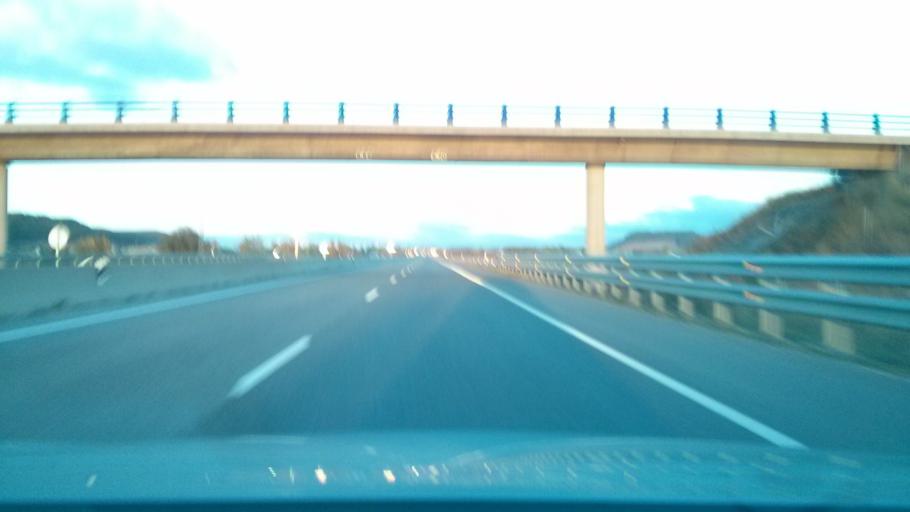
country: ES
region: Castille and Leon
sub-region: Provincia de Burgos
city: Villalbilla de Burgos
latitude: 42.3522
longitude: -3.7855
